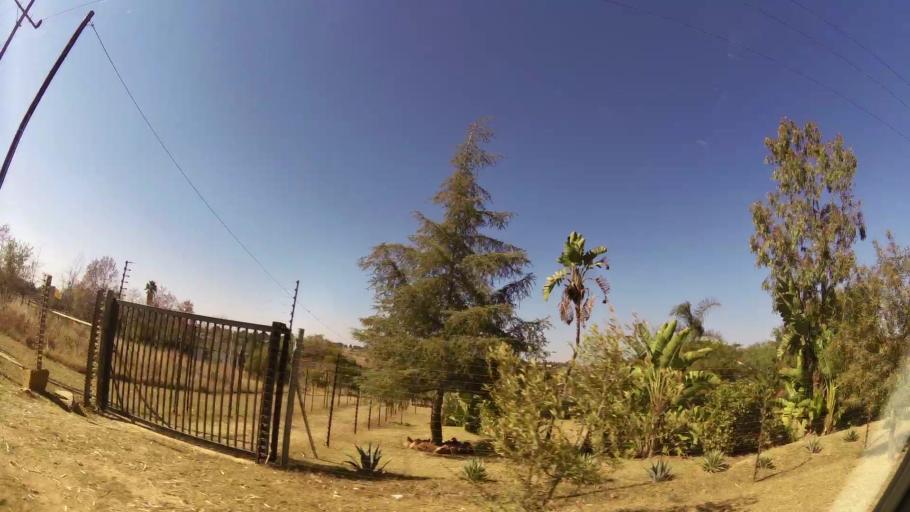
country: ZA
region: Gauteng
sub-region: City of Johannesburg Metropolitan Municipality
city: Midrand
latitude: -25.9386
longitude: 28.0864
